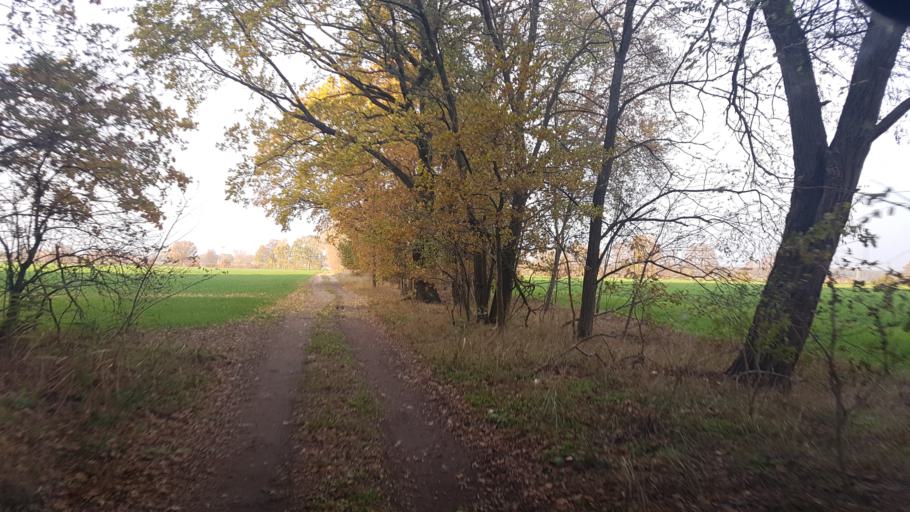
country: DE
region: Brandenburg
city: Schonewalde
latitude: 51.6451
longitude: 13.5999
